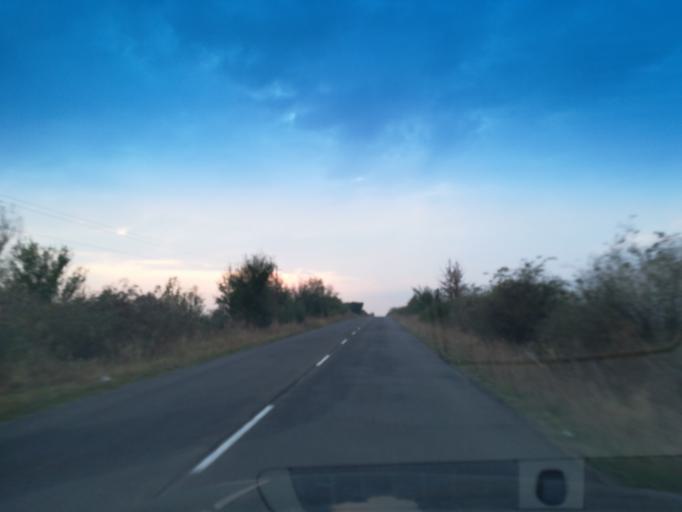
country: BG
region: Stara Zagora
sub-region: Obshtina Chirpan
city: Chirpan
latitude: 42.1841
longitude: 25.2583
